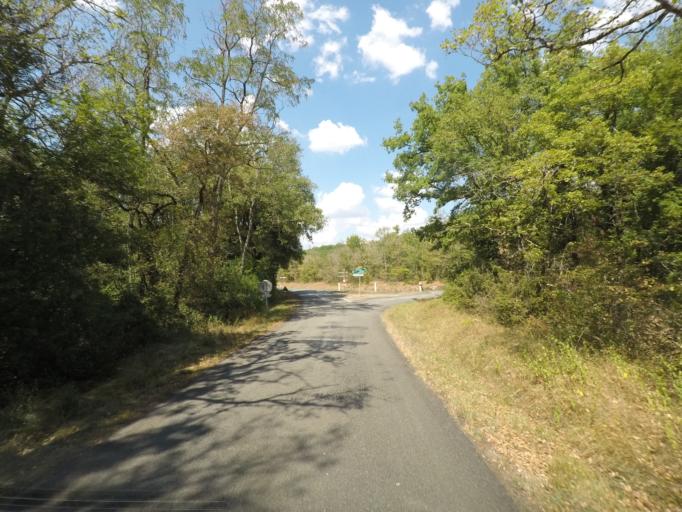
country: FR
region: Midi-Pyrenees
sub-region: Departement du Lot
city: Cahors
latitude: 44.5487
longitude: 1.5932
